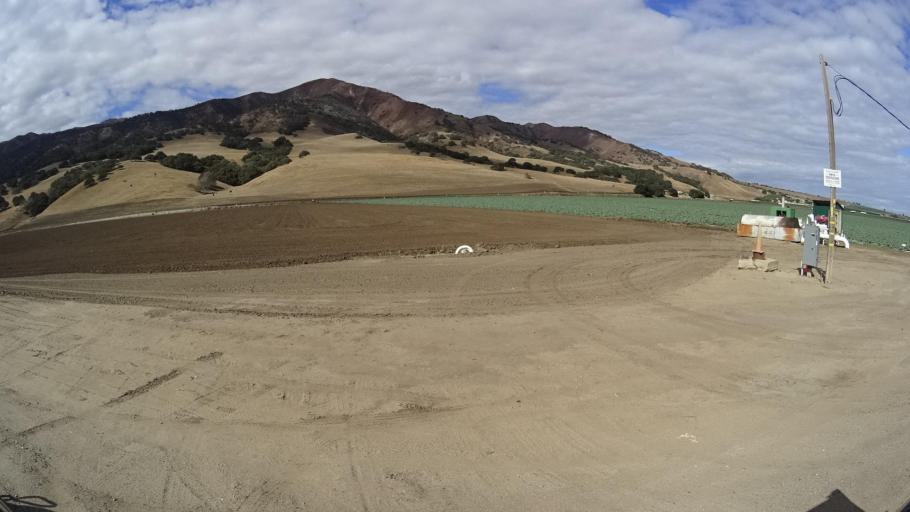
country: US
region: California
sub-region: Monterey County
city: Chualar
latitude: 36.5366
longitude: -121.5402
